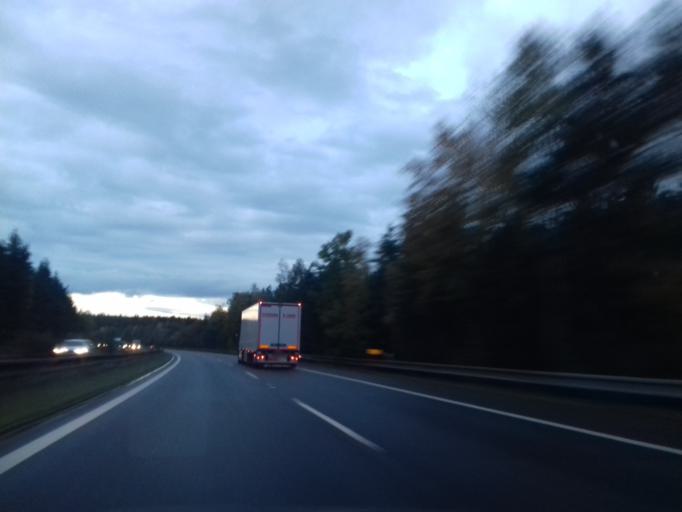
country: CZ
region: Central Bohemia
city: Zruc nad Sazavou
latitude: 49.6797
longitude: 15.1148
